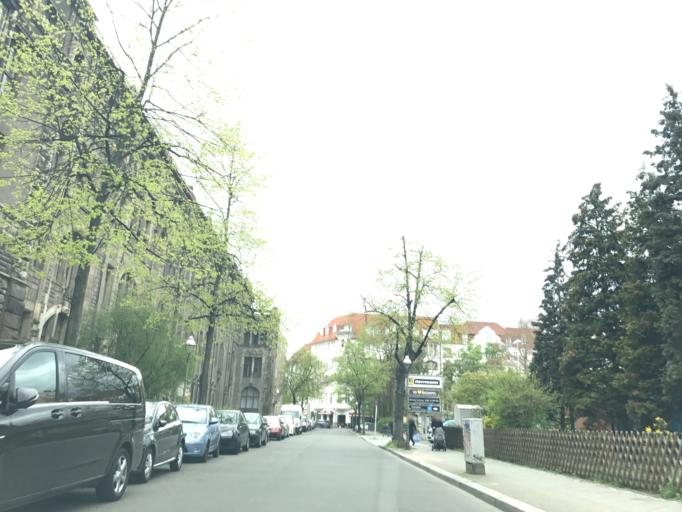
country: DE
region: Berlin
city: Charlottenburg-Nord
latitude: 52.5182
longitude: 13.3099
